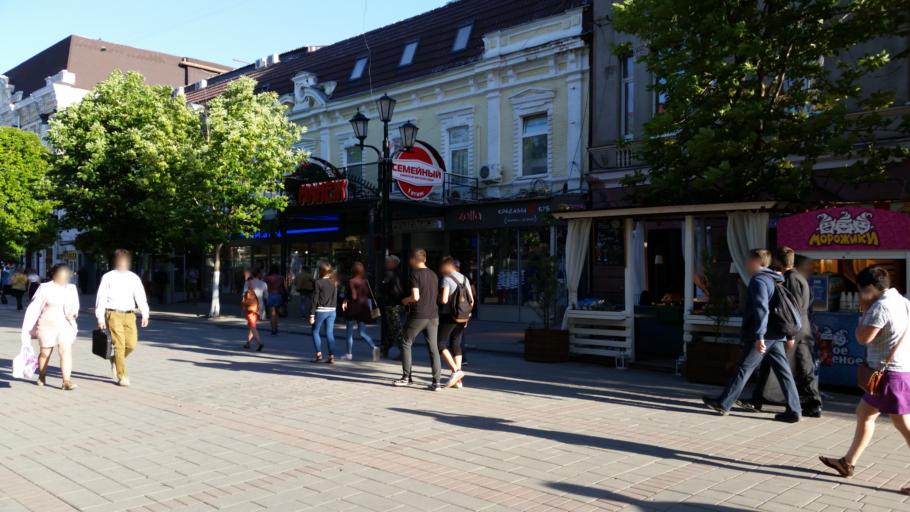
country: RU
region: Saratov
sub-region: Saratovskiy Rayon
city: Saratov
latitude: 51.5317
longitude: 46.0265
